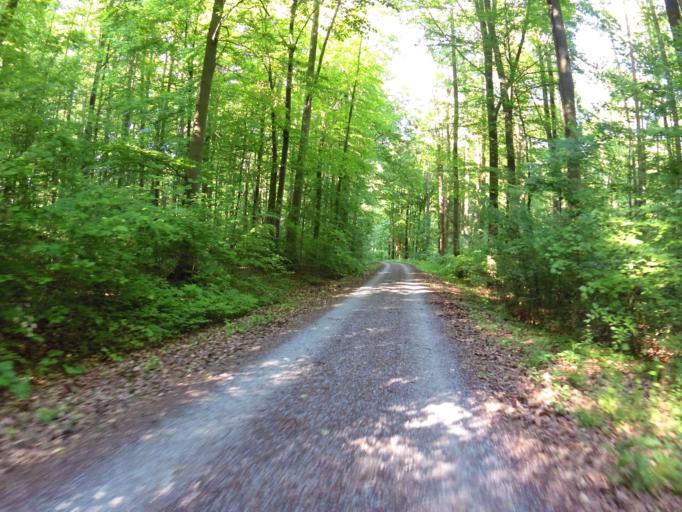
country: DE
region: Bavaria
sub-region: Regierungsbezirk Unterfranken
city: Reichenberg
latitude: 49.7500
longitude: 9.9056
